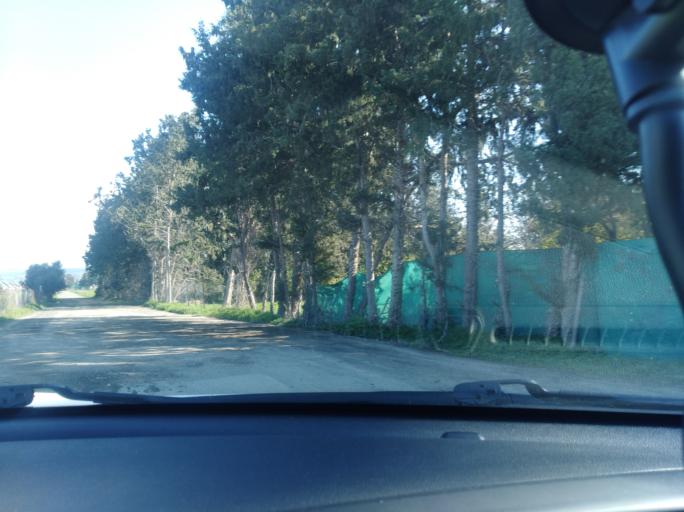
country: CY
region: Pafos
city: Paphos
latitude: 34.7379
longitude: 32.4446
